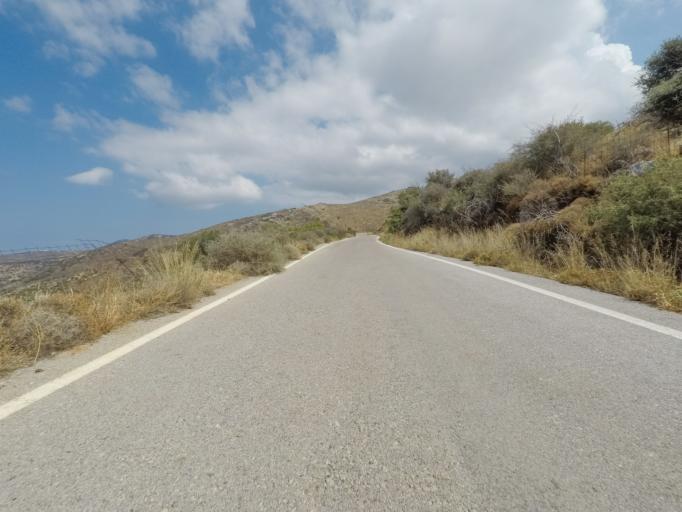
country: GR
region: Crete
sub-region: Nomos Lasithiou
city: Elounda
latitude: 35.3178
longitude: 25.6754
